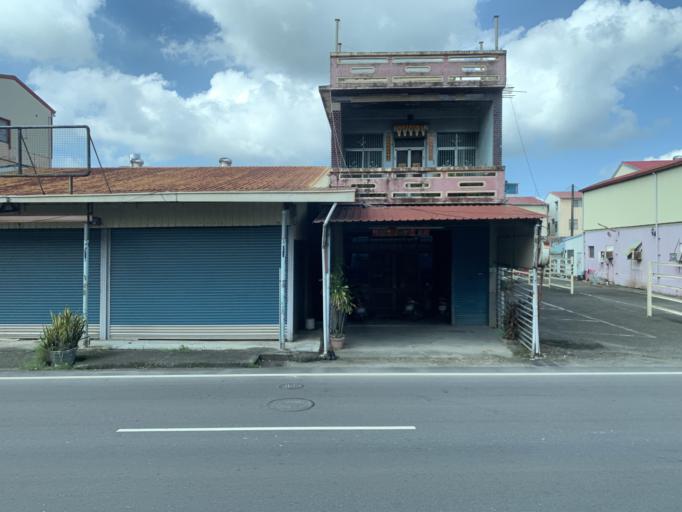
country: TW
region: Taiwan
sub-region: Pingtung
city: Pingtung
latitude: 22.8808
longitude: 120.4959
